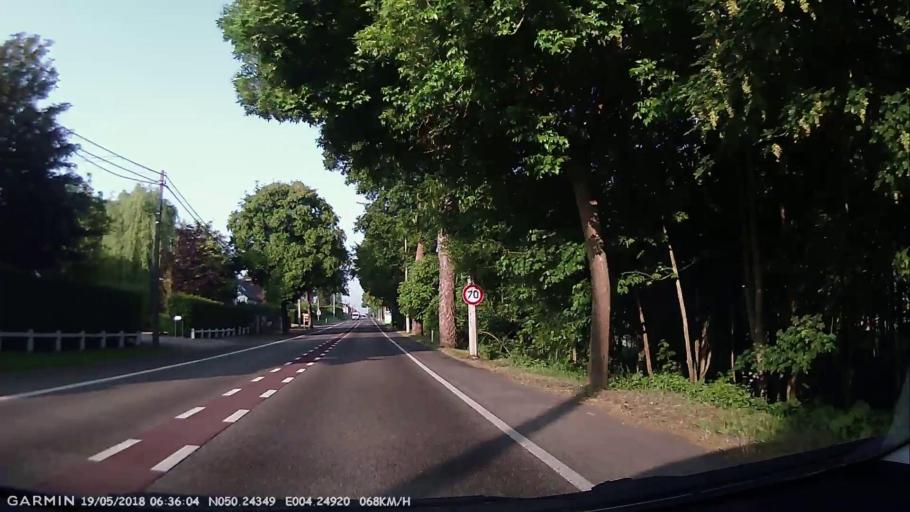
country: BE
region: Wallonia
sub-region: Province du Hainaut
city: Beaumont
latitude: 50.2433
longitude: 4.2490
